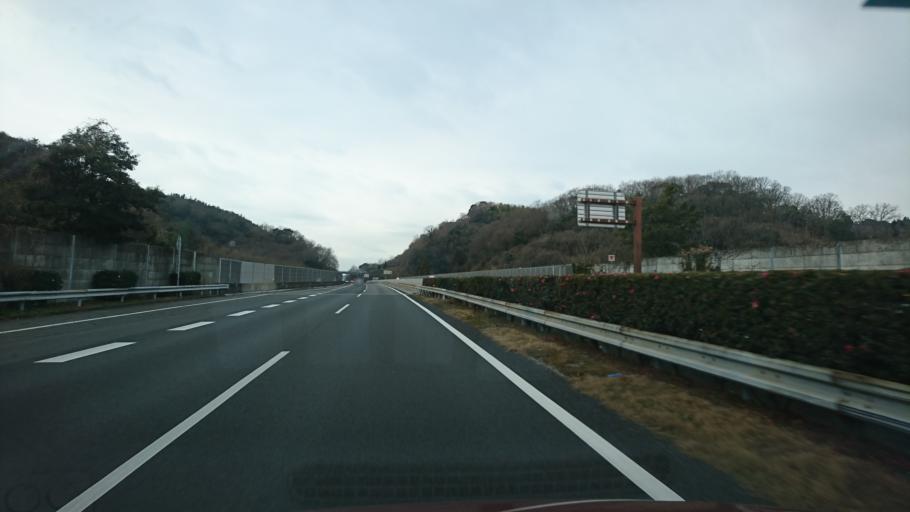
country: JP
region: Okayama
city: Kurashiki
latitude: 34.6260
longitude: 133.7655
